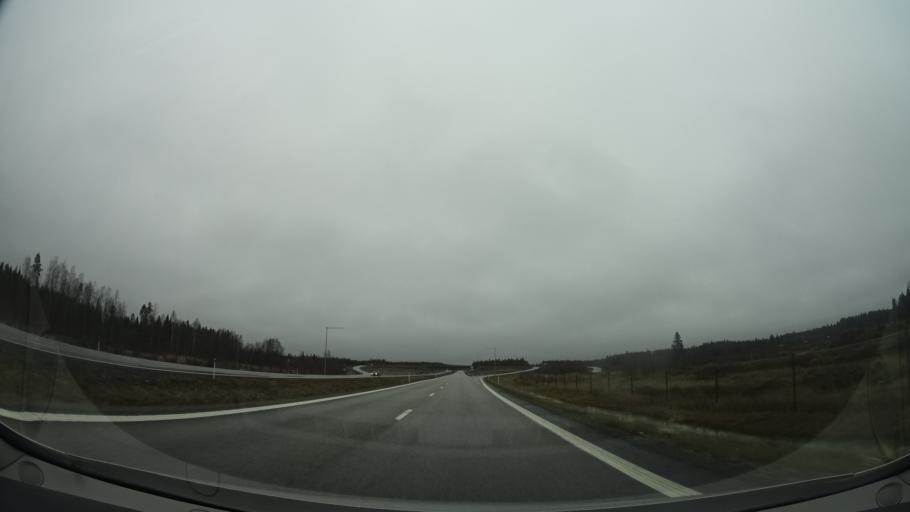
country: SE
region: Vaesterbotten
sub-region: Skelleftea Kommun
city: Kage
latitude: 64.7850
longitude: 21.0193
